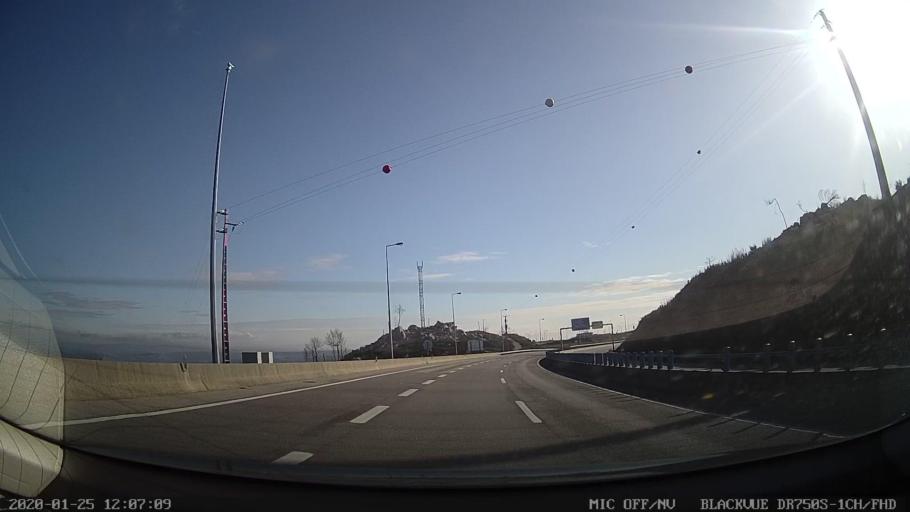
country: PT
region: Viseu
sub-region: Vouzela
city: Vouzela
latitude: 40.6949
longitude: -8.0833
